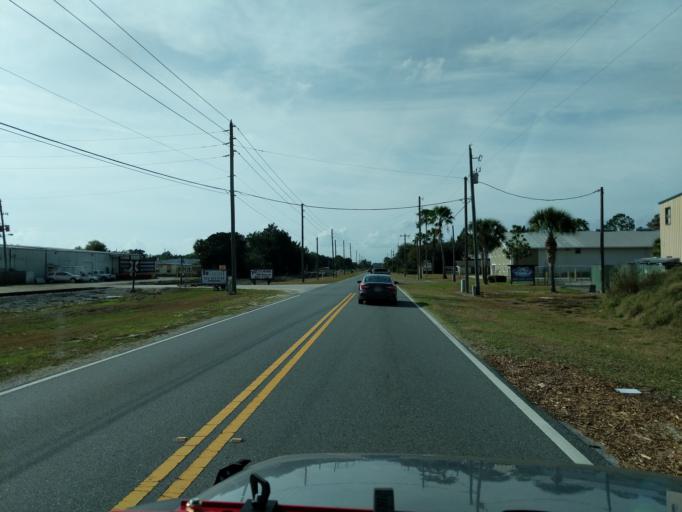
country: US
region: Florida
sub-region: Lake County
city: Tavares
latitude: 28.8035
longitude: -81.6911
